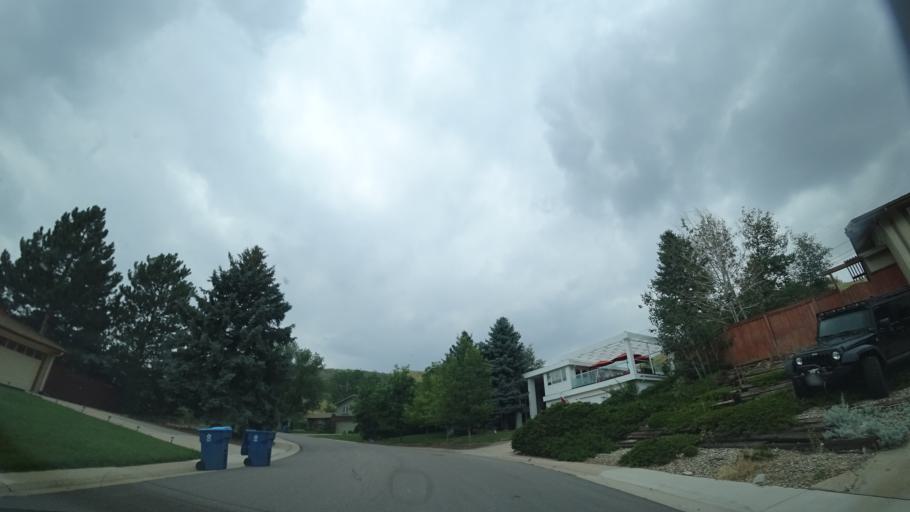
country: US
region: Colorado
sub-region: Jefferson County
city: West Pleasant View
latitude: 39.6956
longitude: -105.1512
